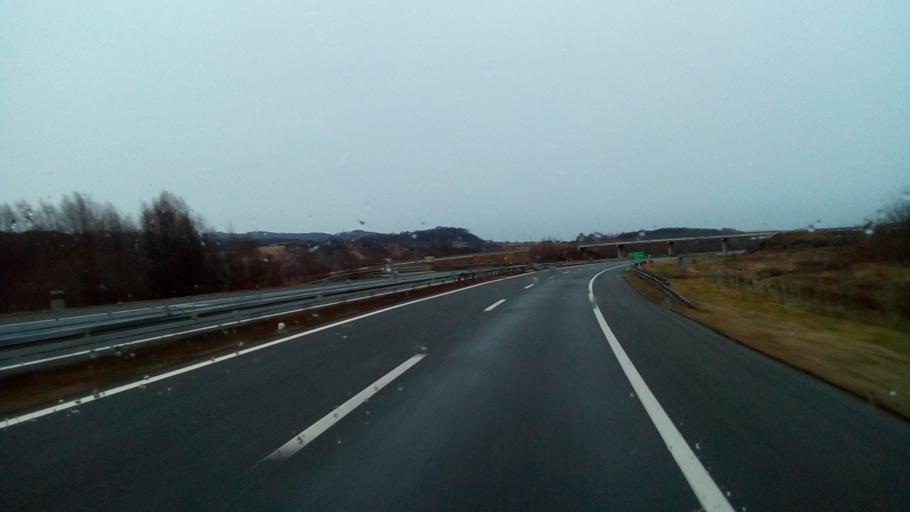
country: HR
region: Varazdinska
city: Ljubescica
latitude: 46.1770
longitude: 16.3776
